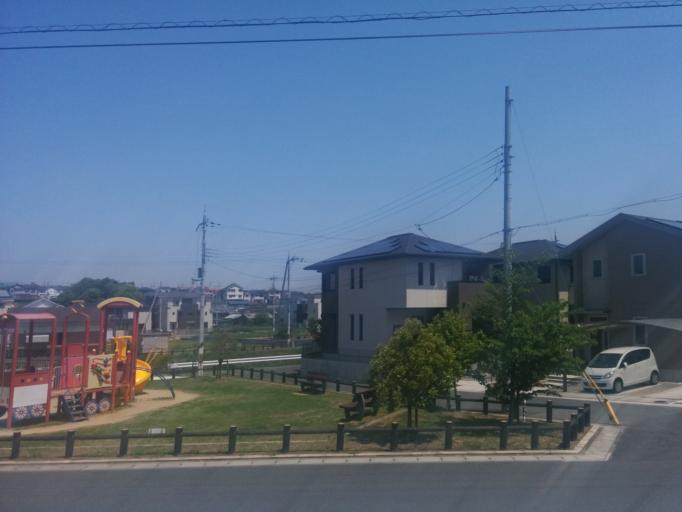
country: JP
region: Nara
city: Tawaramoto
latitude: 34.5393
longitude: 135.7113
